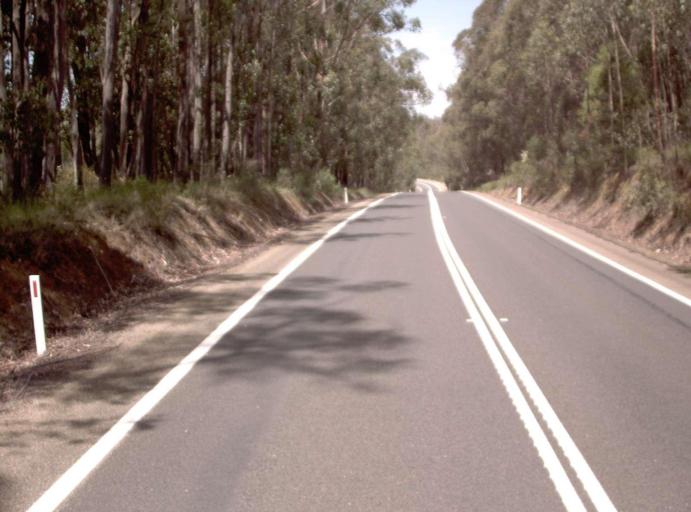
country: AU
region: New South Wales
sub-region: Bombala
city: Bombala
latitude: -37.5365
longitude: 149.3965
